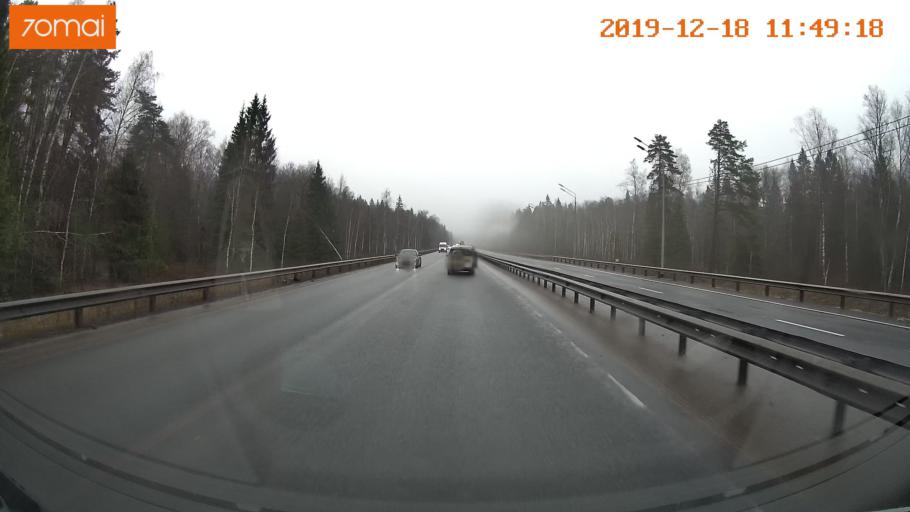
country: RU
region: Moskovskaya
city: Yershovo
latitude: 55.7763
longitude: 36.9106
